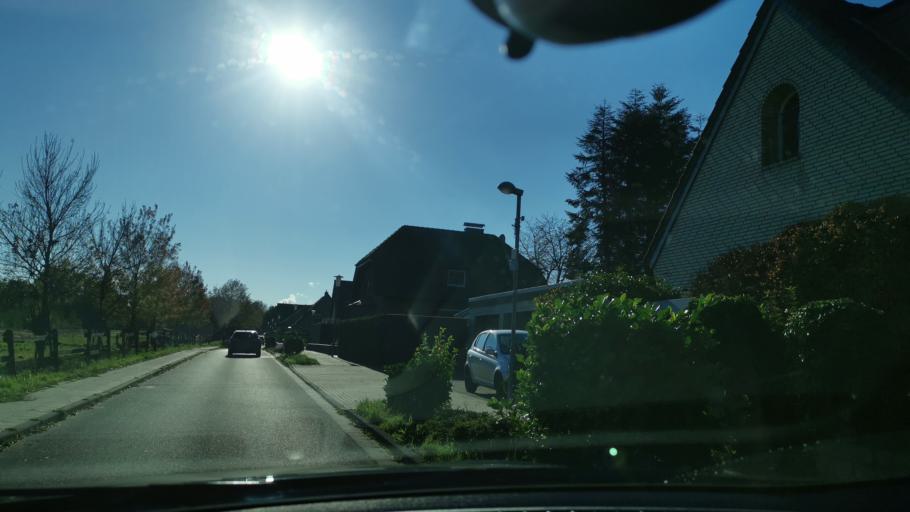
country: DE
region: North Rhine-Westphalia
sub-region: Regierungsbezirk Dusseldorf
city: Rommerskirchen
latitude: 51.0591
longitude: 6.7119
